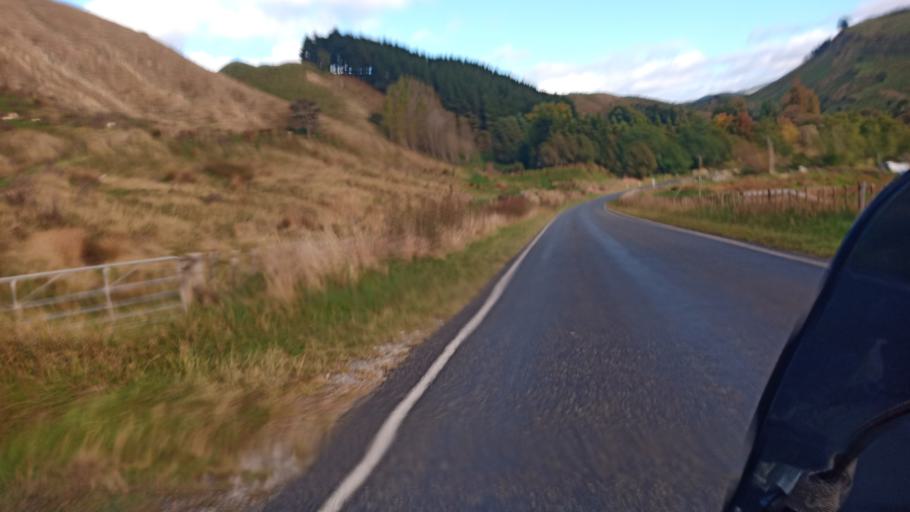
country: NZ
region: Gisborne
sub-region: Gisborne District
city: Gisborne
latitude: -38.5402
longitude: 177.5890
